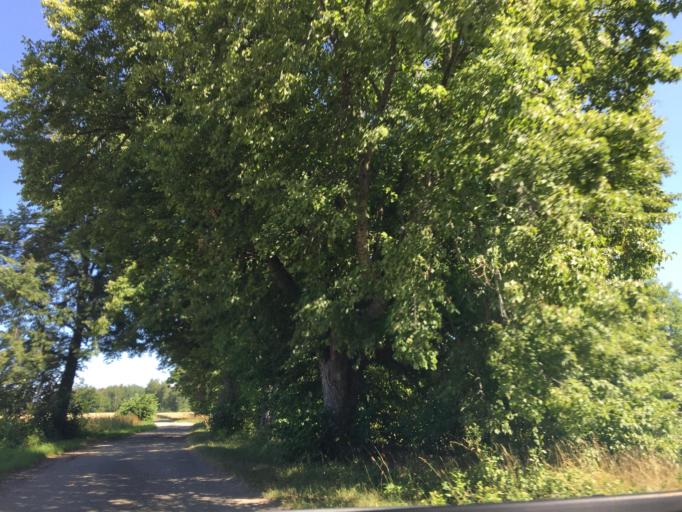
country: LV
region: Talsu Rajons
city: Stende
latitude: 57.1602
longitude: 22.2947
